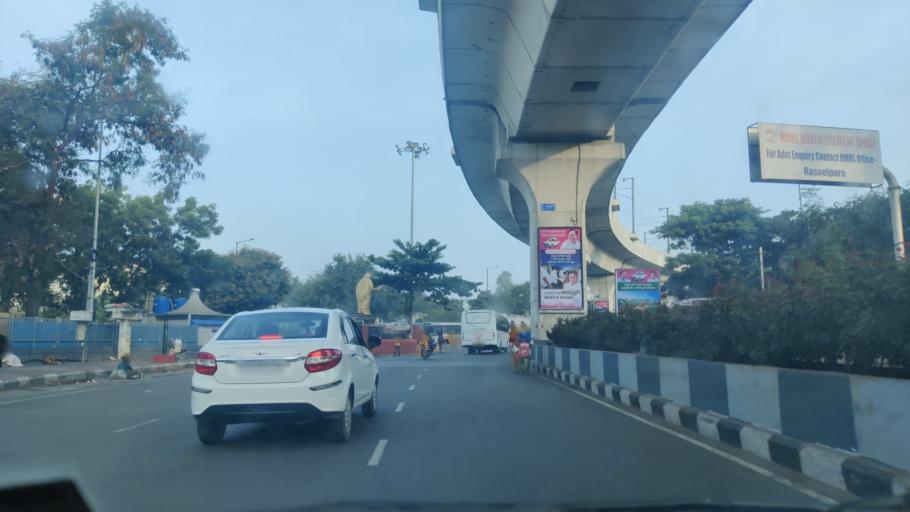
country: IN
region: Telangana
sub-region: Hyderabad
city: Malkajgiri
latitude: 17.4373
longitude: 78.5049
